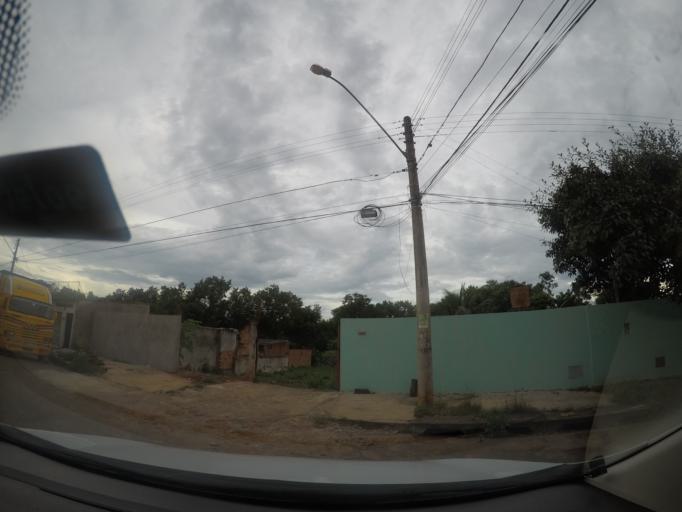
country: BR
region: Goias
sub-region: Goiania
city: Goiania
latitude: -16.6519
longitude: -49.2390
